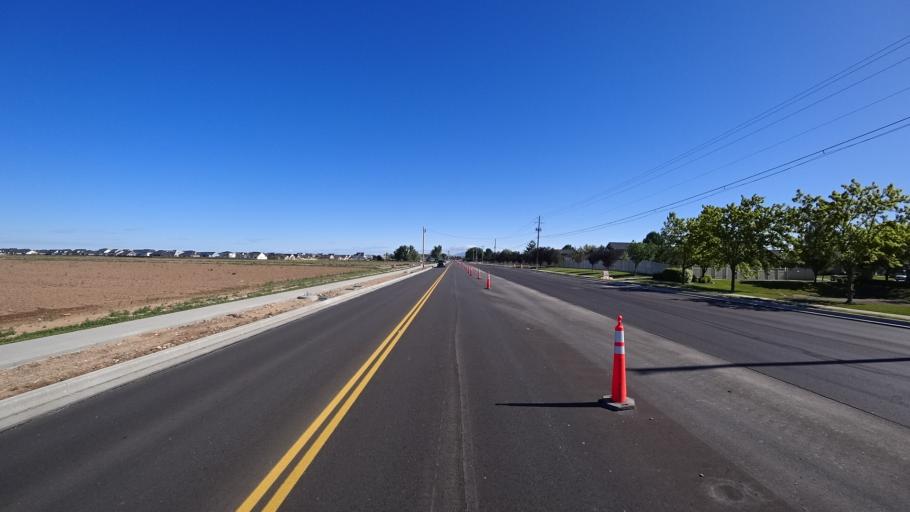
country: US
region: Idaho
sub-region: Ada County
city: Meridian
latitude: 43.6527
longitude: -116.4337
